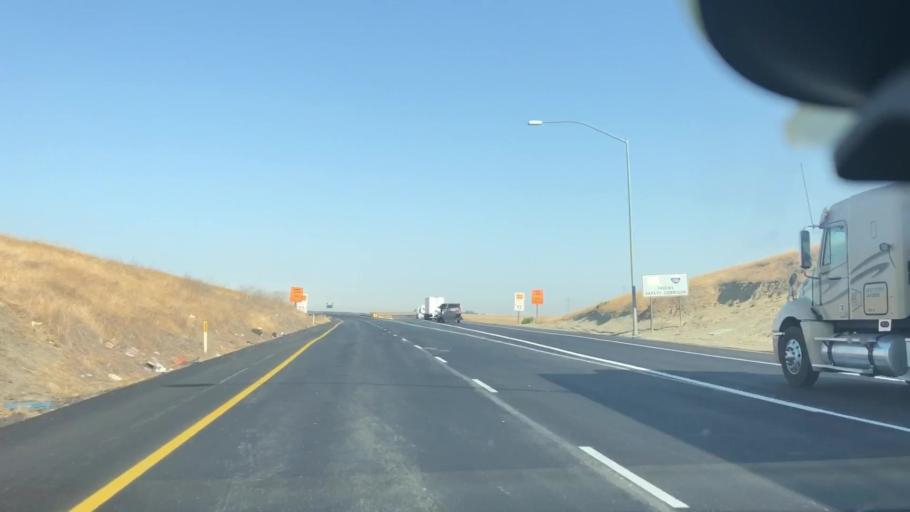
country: US
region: California
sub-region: San Joaquin County
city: Mountain House
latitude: 37.7397
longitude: -121.5580
